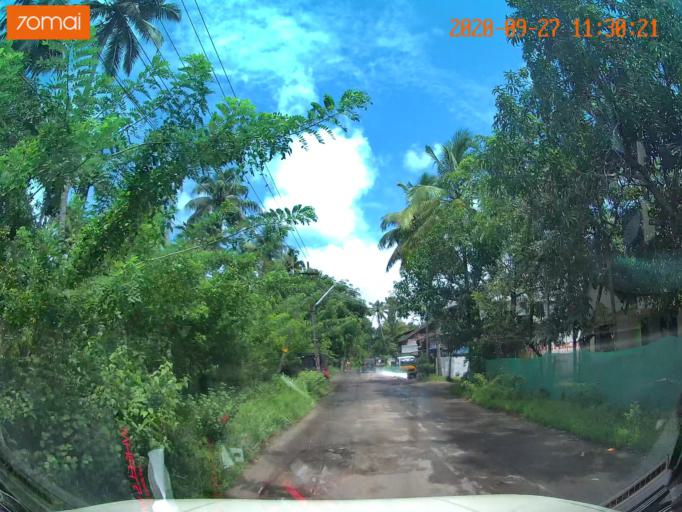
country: IN
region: Kerala
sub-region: Thrissur District
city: Thanniyam
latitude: 10.4191
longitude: 76.1341
